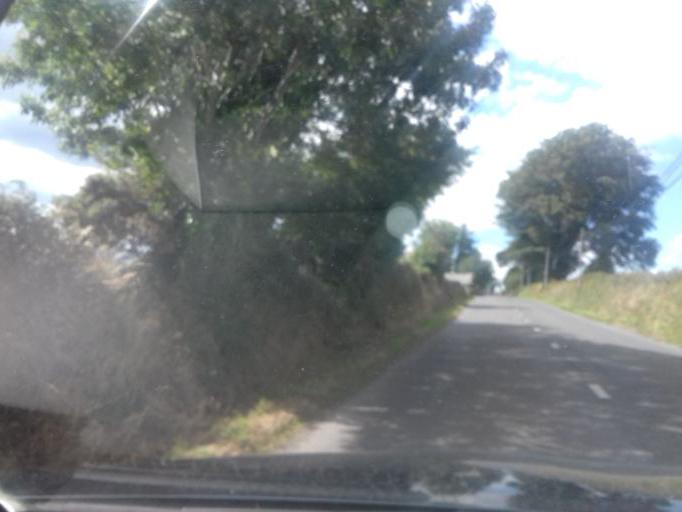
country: IE
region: Munster
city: Carrick-on-Suir
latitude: 52.2856
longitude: -7.4541
